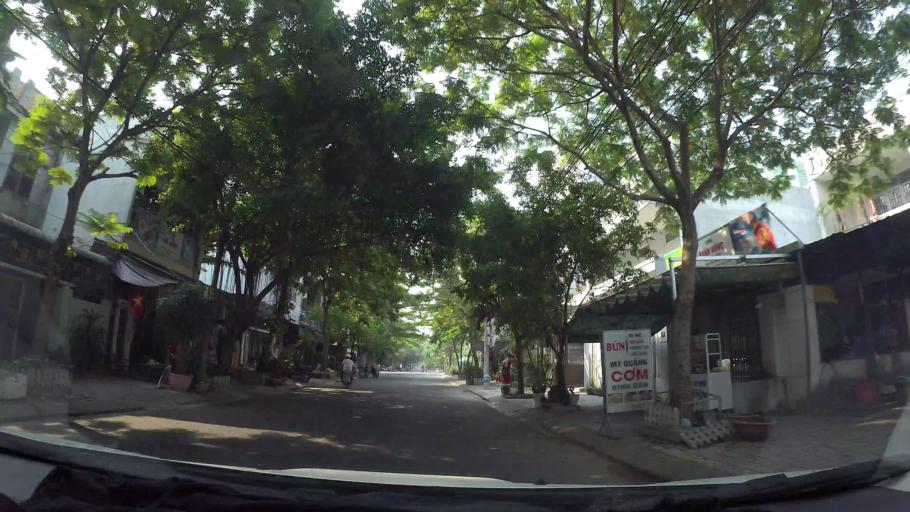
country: VN
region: Da Nang
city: Cam Le
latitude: 16.0020
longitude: 108.2148
